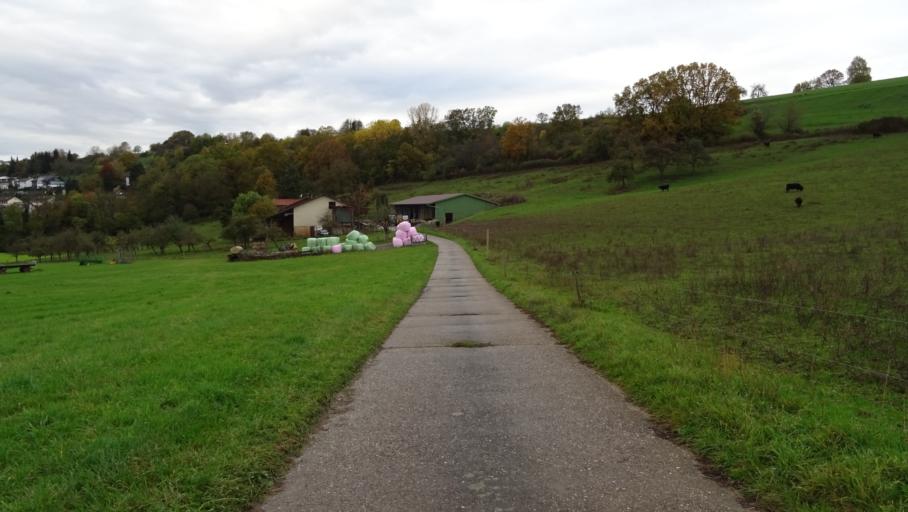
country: DE
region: Baden-Wuerttemberg
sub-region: Karlsruhe Region
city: Obrigheim
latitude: 49.3741
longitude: 9.0873
